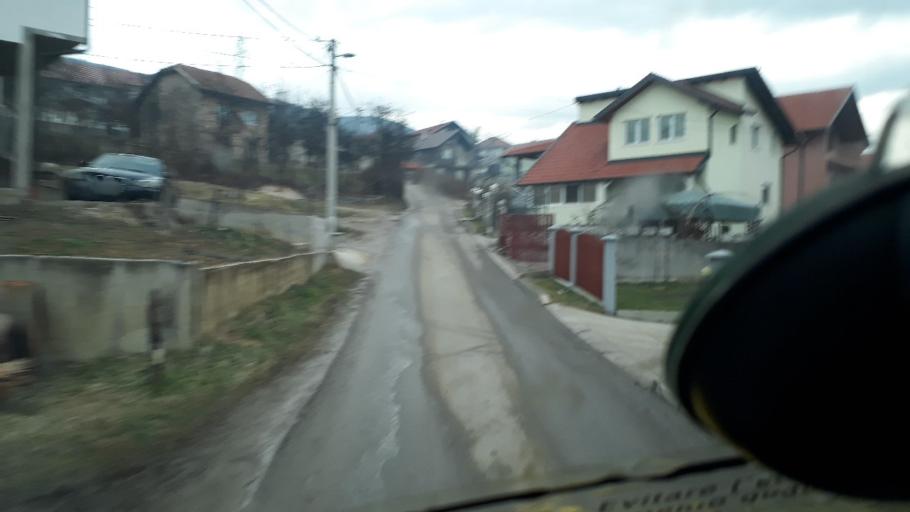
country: BA
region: Federation of Bosnia and Herzegovina
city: Zenica
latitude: 44.1928
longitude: 17.9507
